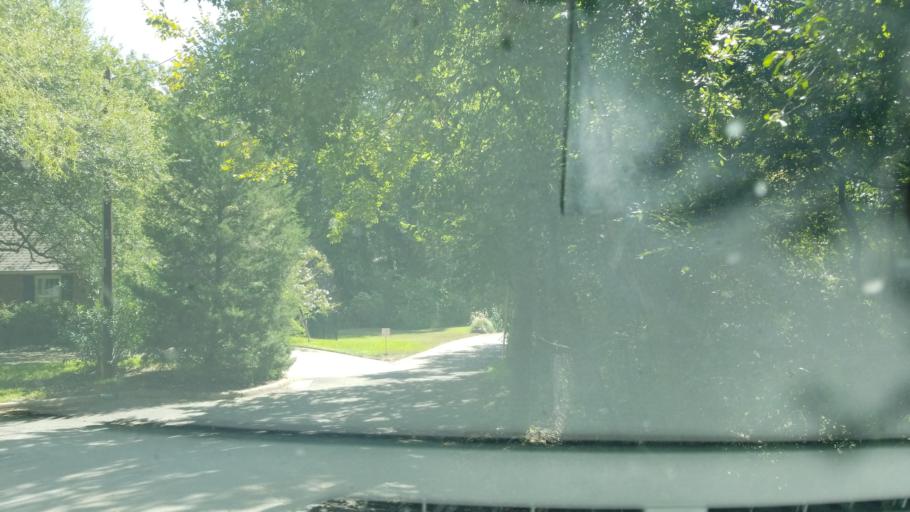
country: US
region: Texas
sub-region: Dallas County
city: Dallas
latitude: 32.7601
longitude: -96.8327
